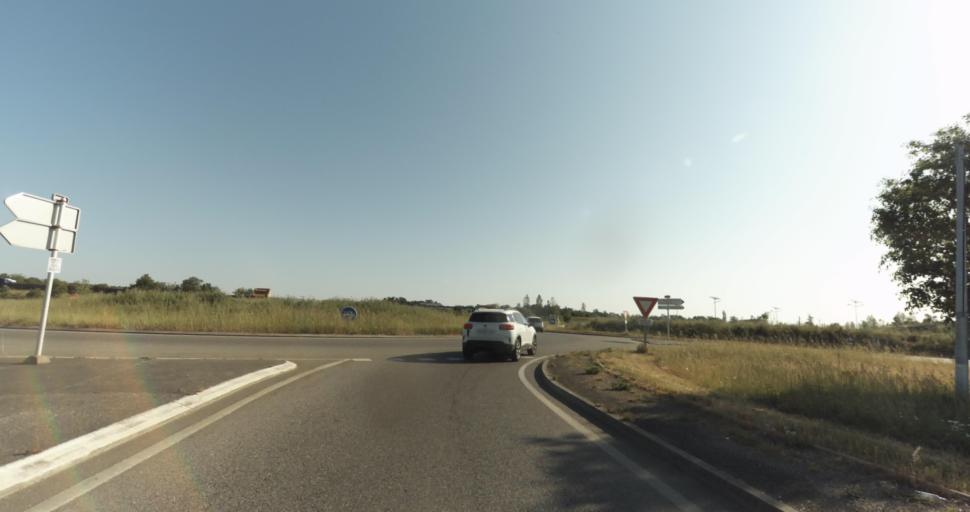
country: FR
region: Midi-Pyrenees
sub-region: Departement de la Haute-Garonne
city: Leguevin
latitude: 43.5803
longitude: 1.2177
